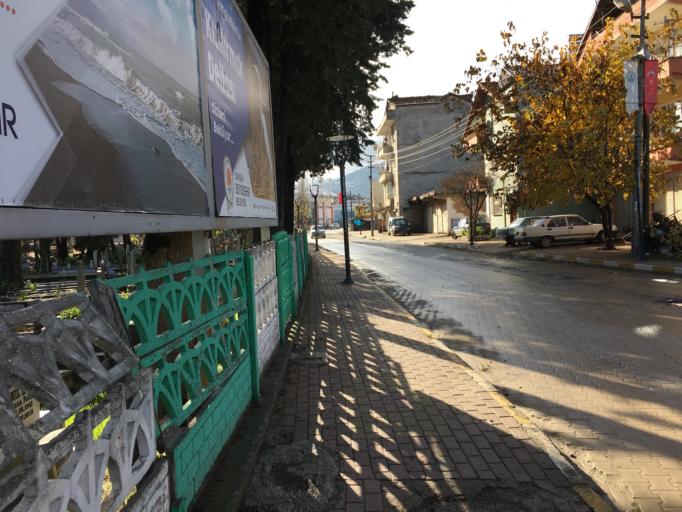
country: TR
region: Samsun
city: Alacam
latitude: 41.6146
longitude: 35.6028
